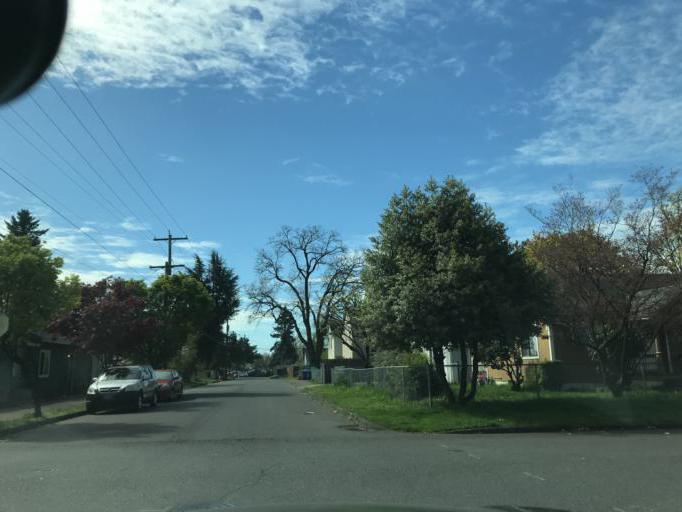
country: US
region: Oregon
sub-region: Multnomah County
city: Lents
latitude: 45.4963
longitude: -122.5764
